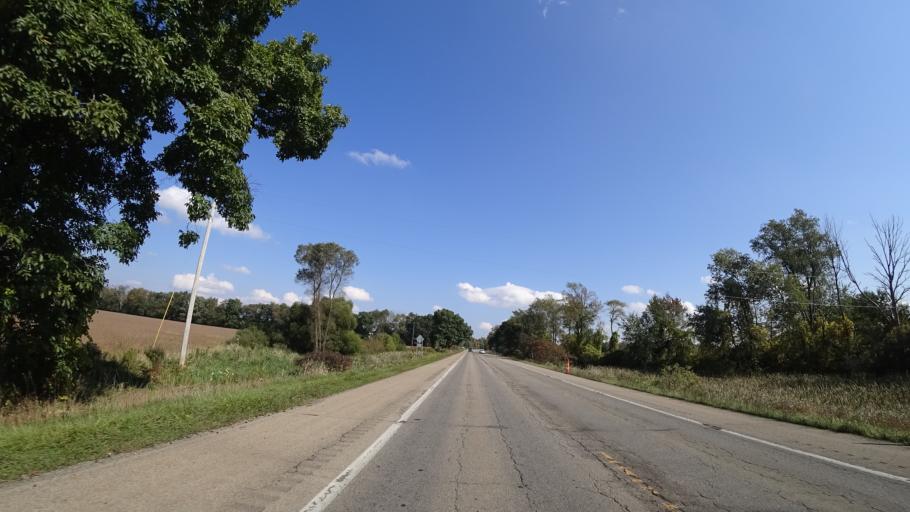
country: US
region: Michigan
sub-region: Calhoun County
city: Homer
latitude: 42.1472
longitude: -84.8259
